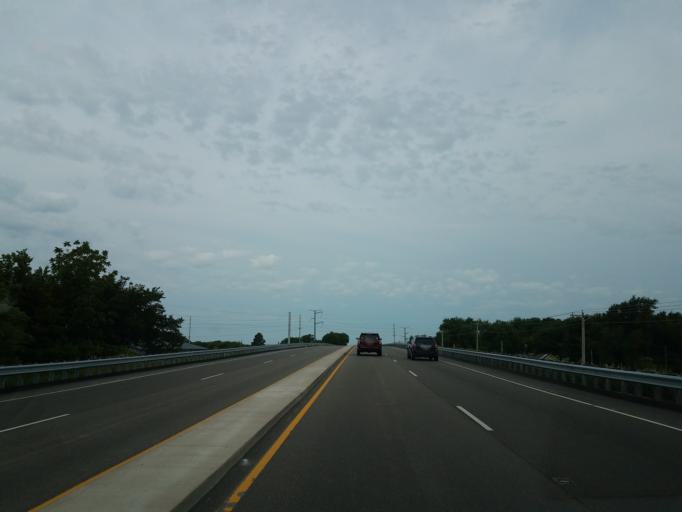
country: US
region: Illinois
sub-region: McLean County
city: Bloomington
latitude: 40.4595
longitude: -88.9798
